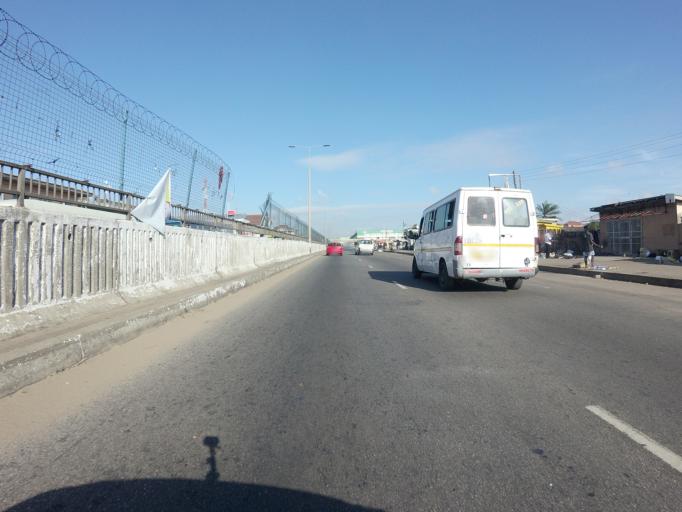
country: GH
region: Greater Accra
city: Accra
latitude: 5.5638
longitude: -0.2334
